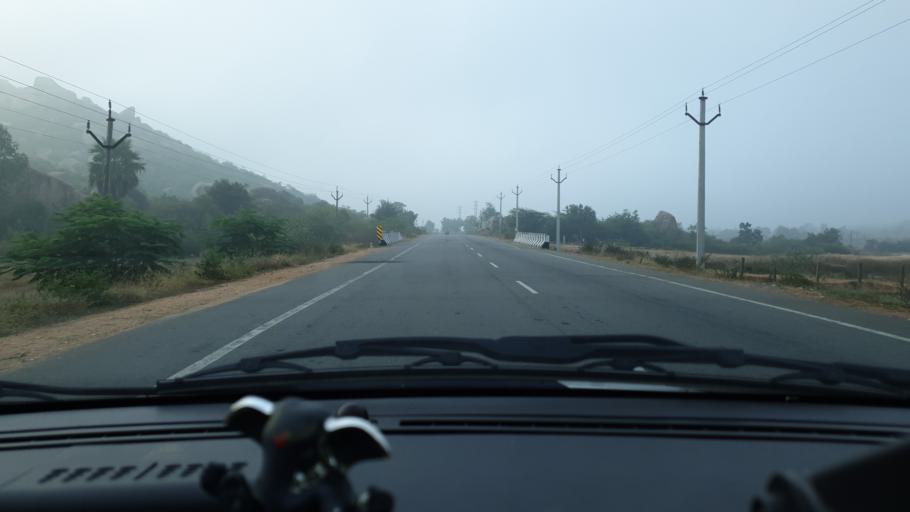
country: IN
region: Telangana
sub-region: Mahbubnagar
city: Farrukhnagar
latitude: 16.8980
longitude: 78.5303
